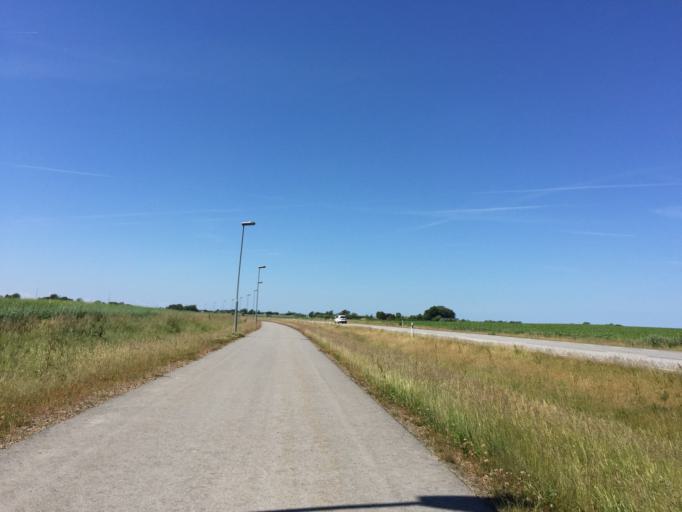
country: SE
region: Skane
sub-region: Trelleborgs Kommun
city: Trelleborg
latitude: 55.3877
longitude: 13.1050
